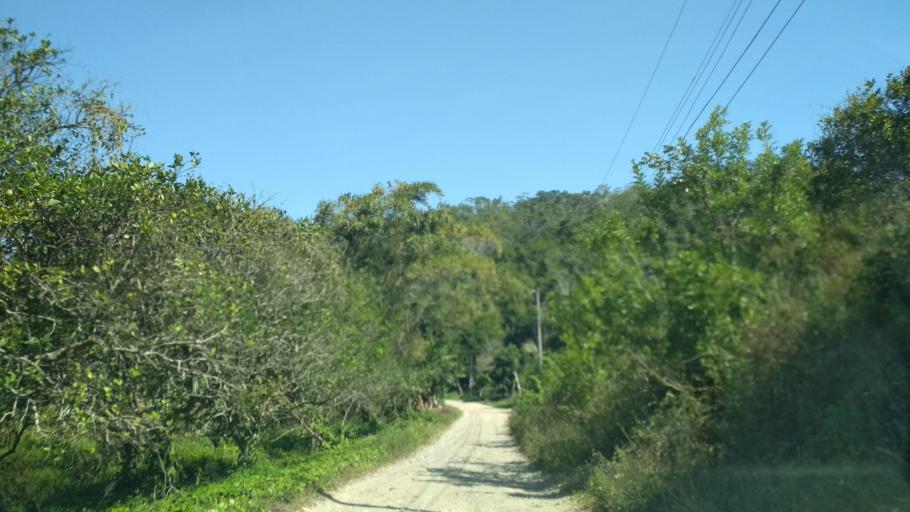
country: MX
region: Veracruz
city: Gutierrez Zamora
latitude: 20.4833
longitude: -97.1615
